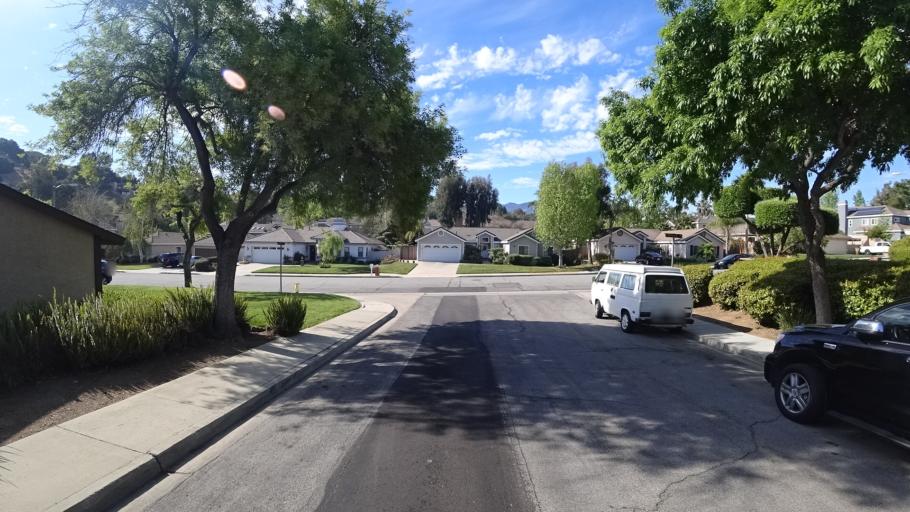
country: US
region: California
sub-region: Ventura County
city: Casa Conejo
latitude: 34.1749
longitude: -118.9400
